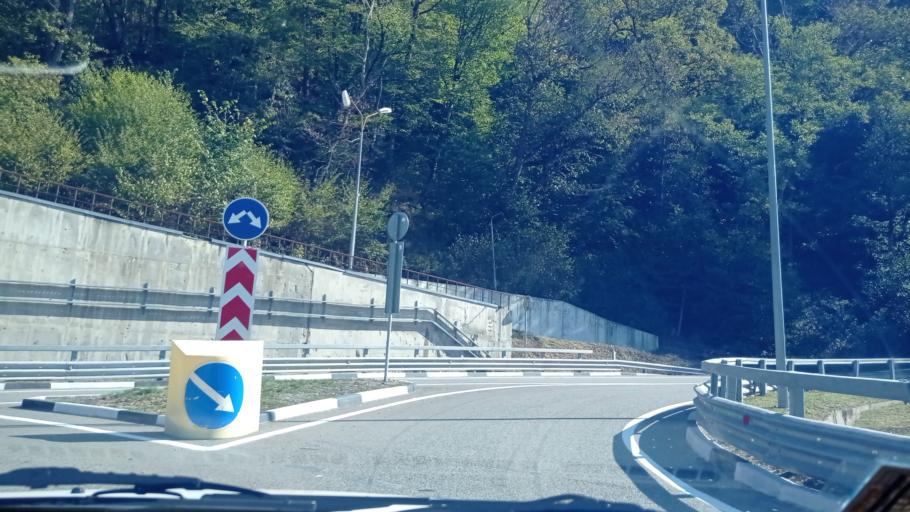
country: RU
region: Krasnodarskiy
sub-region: Sochi City
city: Krasnaya Polyana
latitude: 43.6840
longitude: 40.2454
